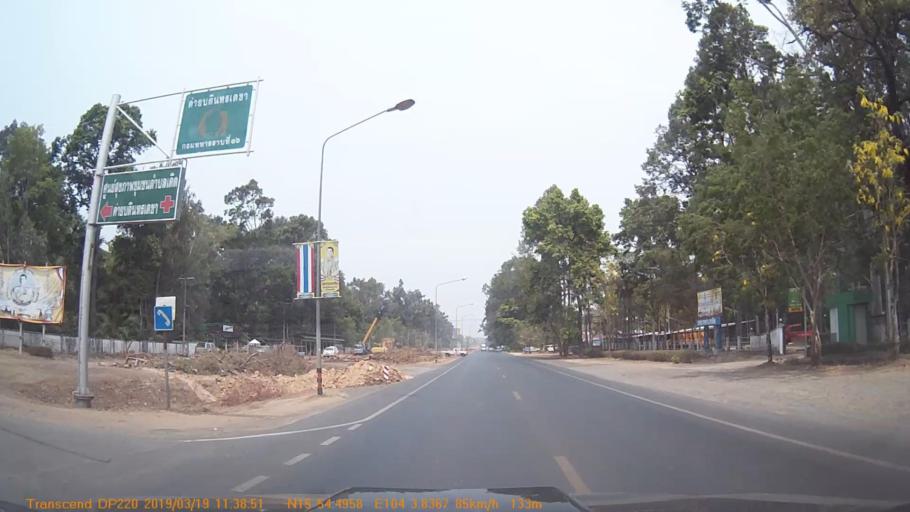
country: TH
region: Yasothon
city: Yasothon
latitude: 15.9085
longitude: 104.0639
